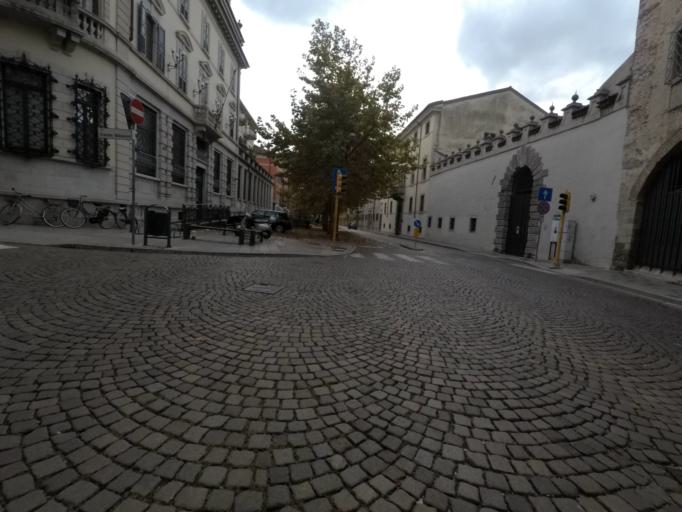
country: IT
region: Friuli Venezia Giulia
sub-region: Provincia di Udine
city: Udine
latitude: 46.0640
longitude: 13.2322
